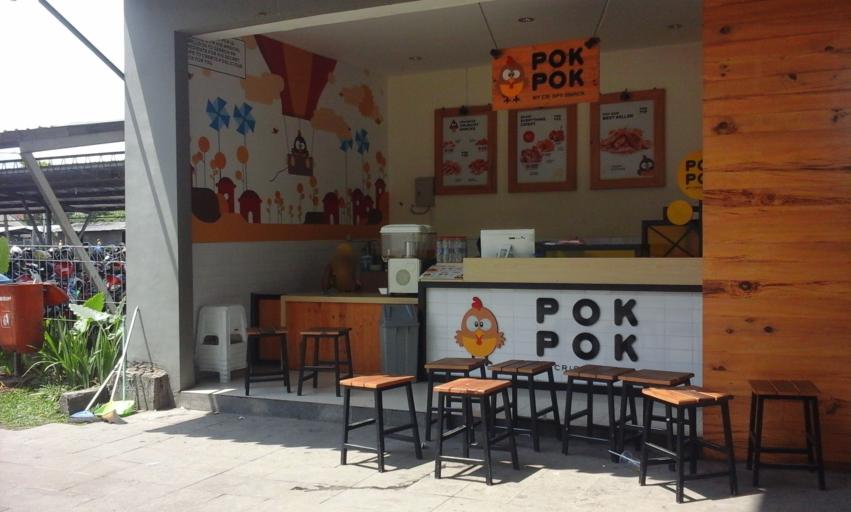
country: ID
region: East Java
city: Krajan
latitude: -8.1844
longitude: 113.6628
